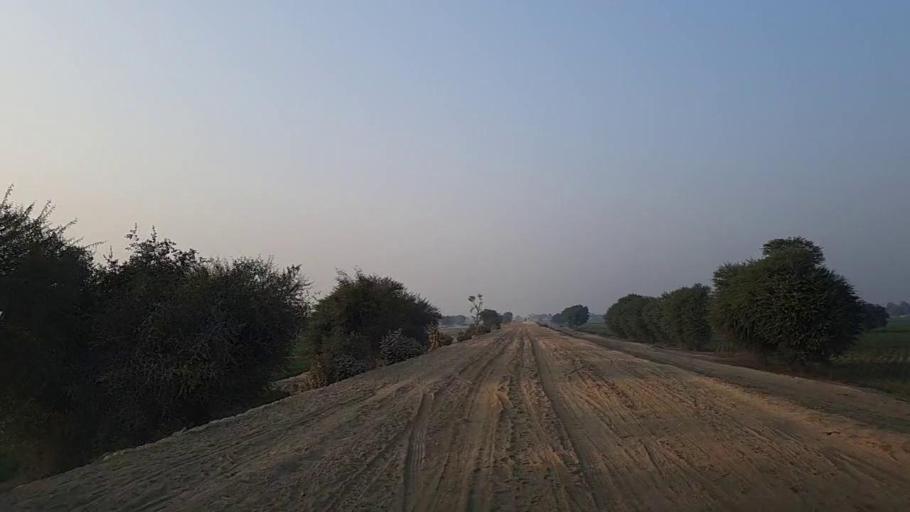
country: PK
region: Sindh
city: Sann
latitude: 26.1831
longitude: 68.0943
